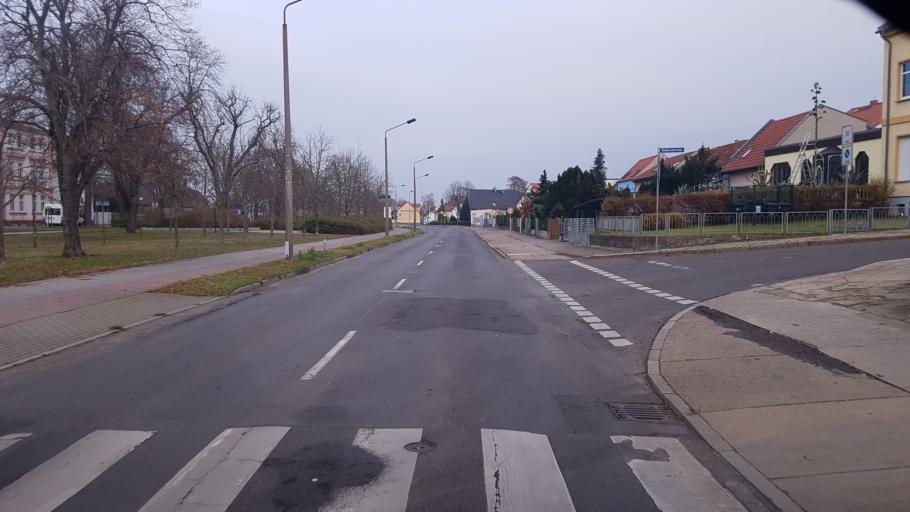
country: DE
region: Brandenburg
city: Eisenhuettenstadt
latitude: 52.1461
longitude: 14.6722
